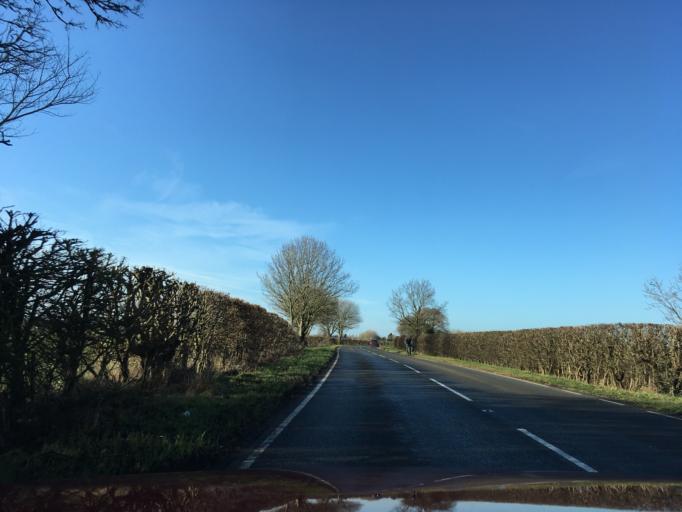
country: GB
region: England
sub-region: Warwickshire
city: Wellesbourne Mountford
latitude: 52.1967
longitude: -1.6087
